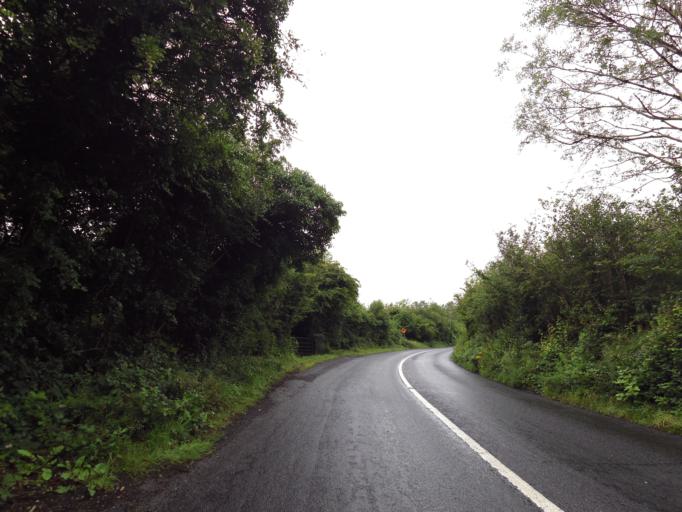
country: IE
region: Connaught
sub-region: County Galway
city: Gaillimh
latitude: 53.2989
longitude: -9.0597
